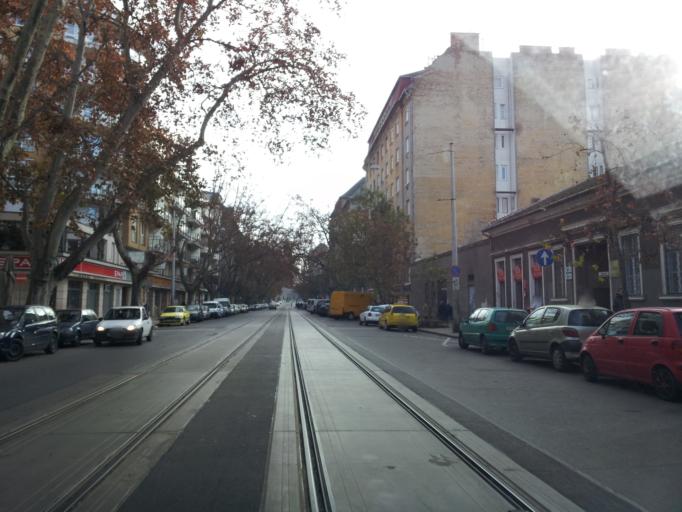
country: HU
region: Budapest
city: Budapest IX. keruelet
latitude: 47.4787
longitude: 19.0736
